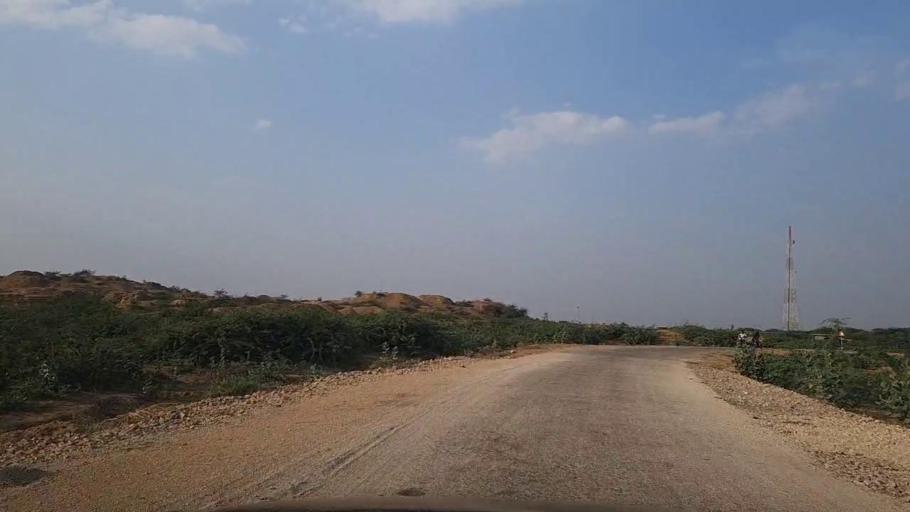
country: PK
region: Sindh
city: Thatta
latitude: 24.8492
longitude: 67.7687
